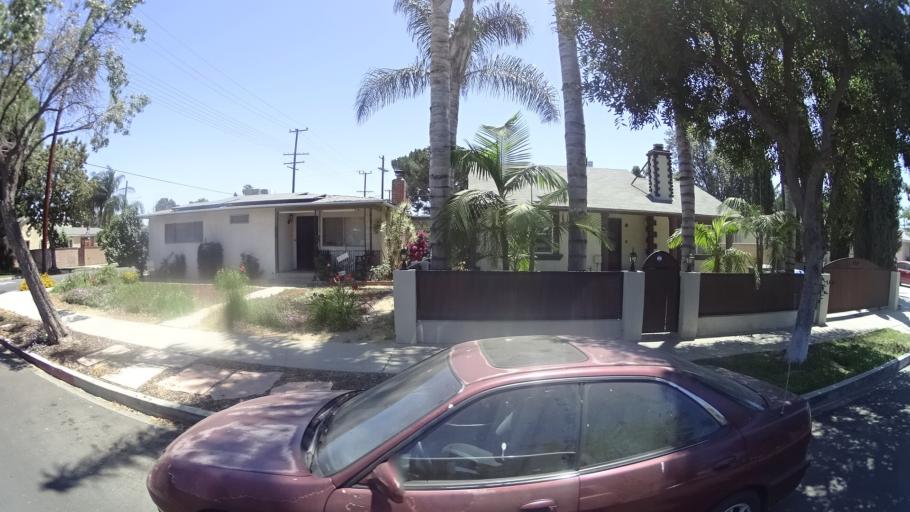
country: US
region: California
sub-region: Los Angeles County
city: Northridge
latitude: 34.1972
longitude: -118.5295
